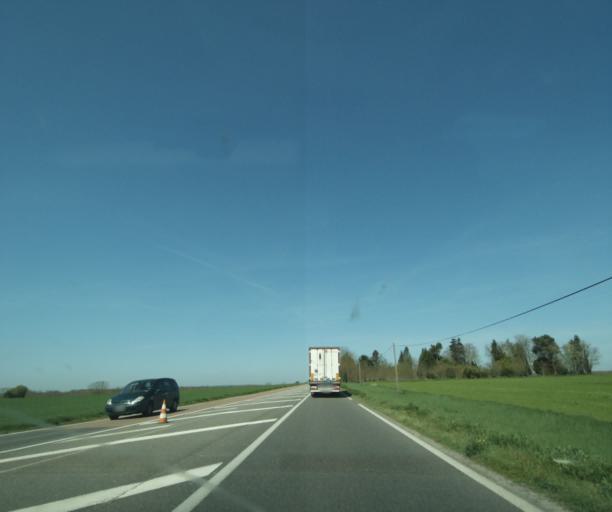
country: FR
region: Bourgogne
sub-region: Departement de la Nievre
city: Chantenay-Saint-Imbert
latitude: 46.7381
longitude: 3.1626
